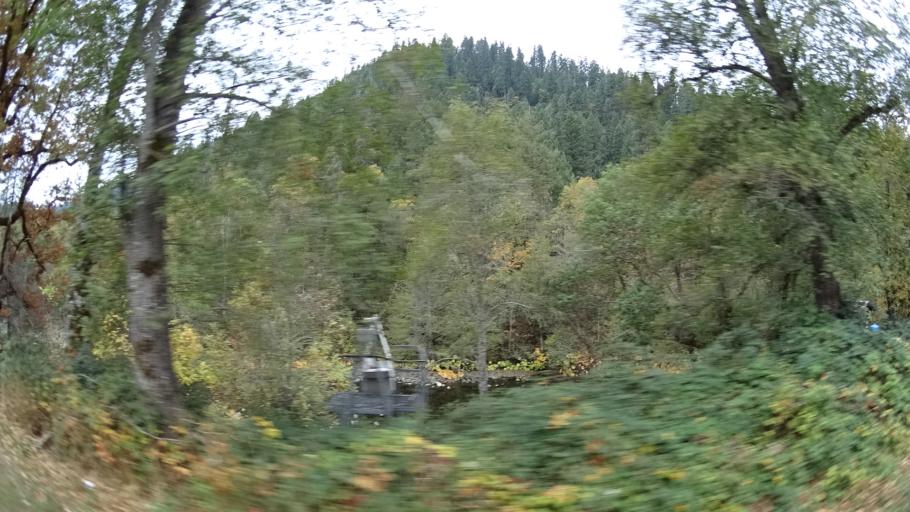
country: US
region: California
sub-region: Siskiyou County
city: Happy Camp
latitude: 41.8356
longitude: -123.3827
